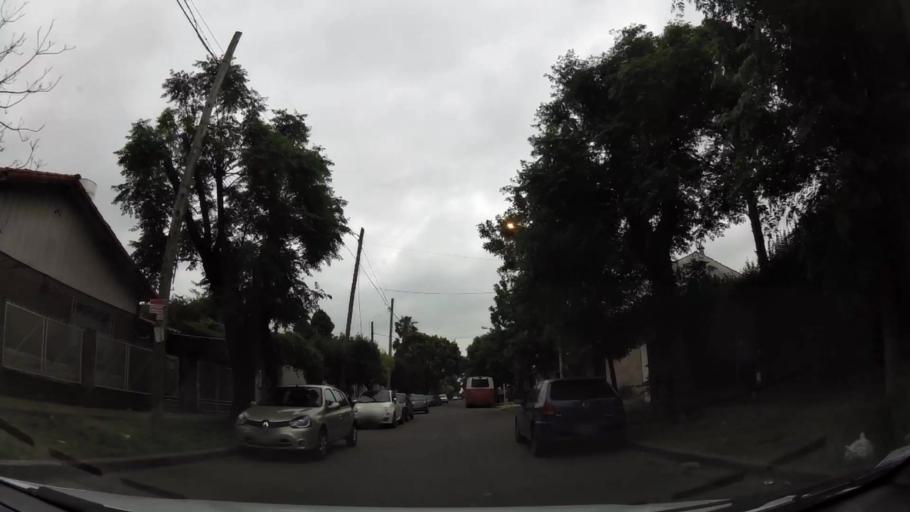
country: AR
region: Buenos Aires
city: San Justo
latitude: -34.7075
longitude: -58.5179
